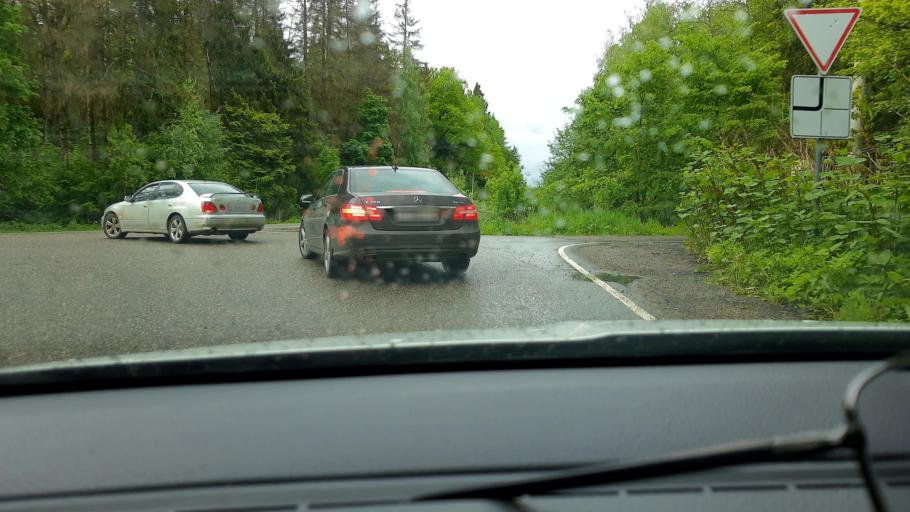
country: RU
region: Moskovskaya
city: Nikolina Gora
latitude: 55.7624
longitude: 36.9823
